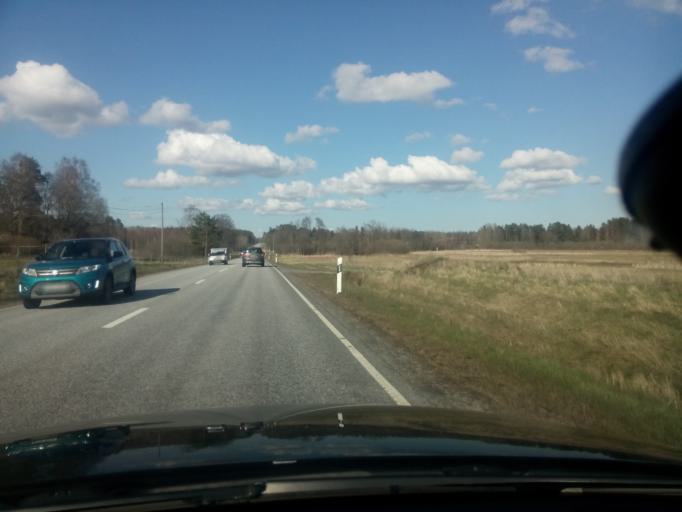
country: SE
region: Soedermanland
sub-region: Strangnas Kommun
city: Strangnas
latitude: 59.3078
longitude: 16.9908
